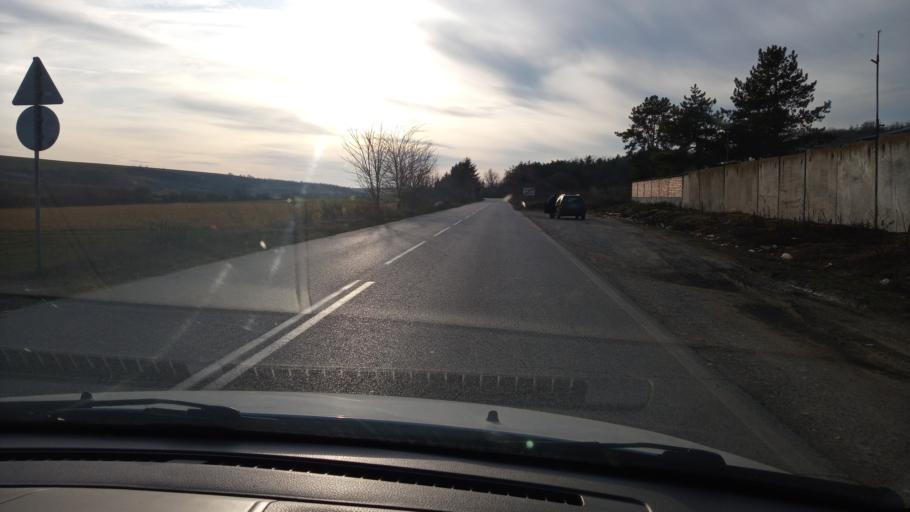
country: BG
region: Pleven
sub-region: Obshtina Pleven
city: Slavyanovo
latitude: 43.5473
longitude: 24.8603
